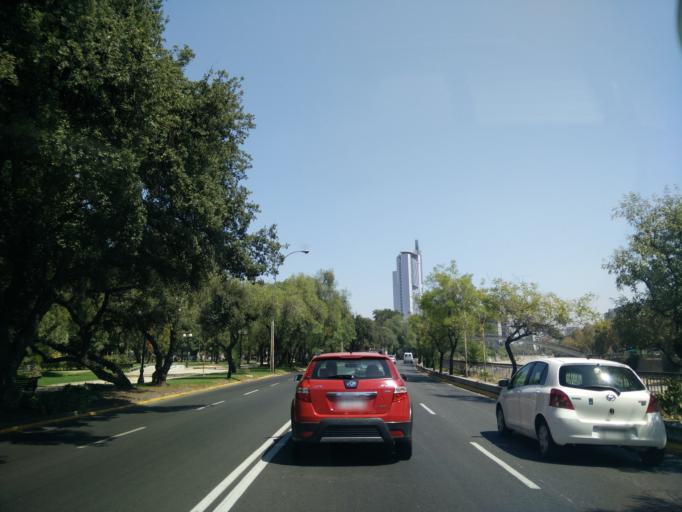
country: CL
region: Santiago Metropolitan
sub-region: Provincia de Santiago
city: Santiago
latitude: -33.4329
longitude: -70.6271
